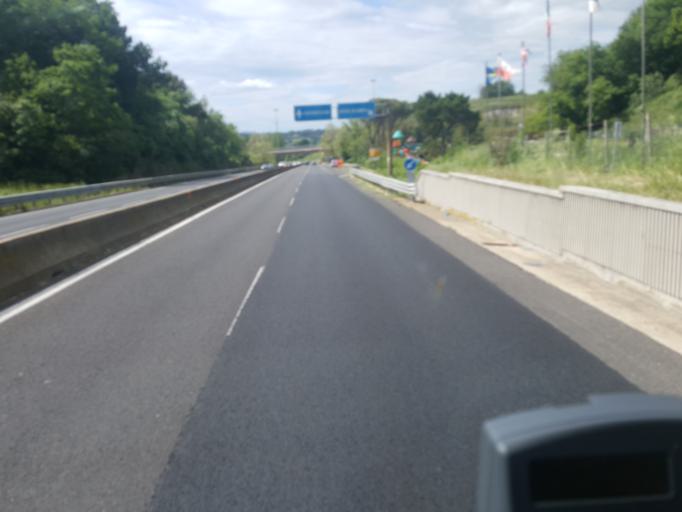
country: IT
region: Latium
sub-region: Citta metropolitana di Roma Capitale
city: Ara Nova
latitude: 41.9007
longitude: 12.2741
